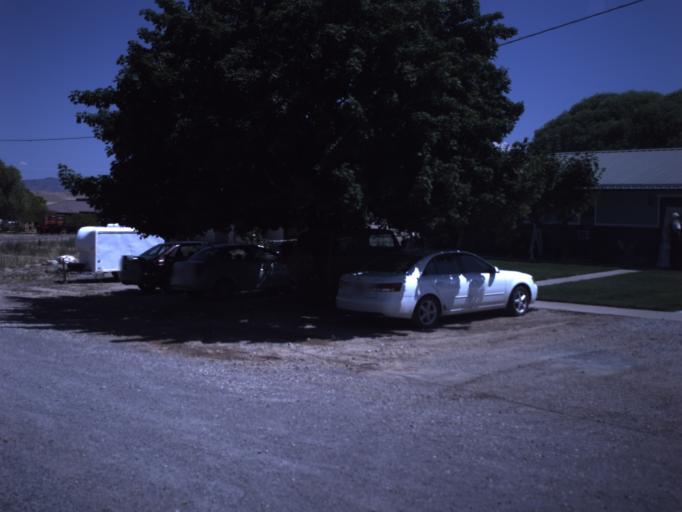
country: US
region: Utah
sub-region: Millard County
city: Delta
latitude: 39.3786
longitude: -112.3360
